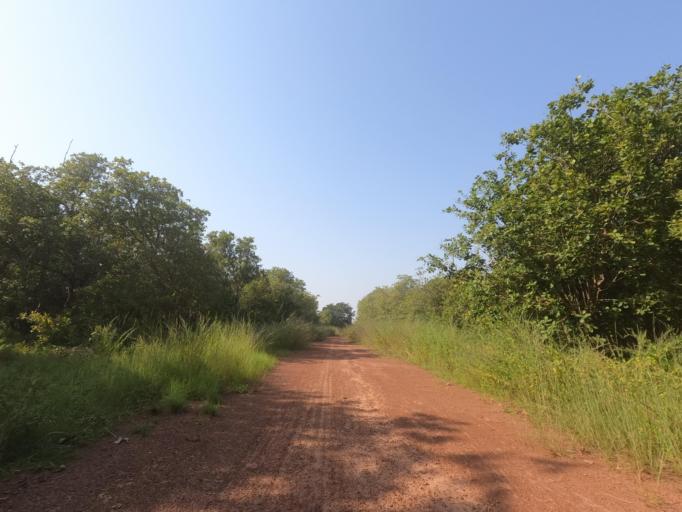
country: SN
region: Sedhiou
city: Sedhiou
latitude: 12.4414
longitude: -15.7383
